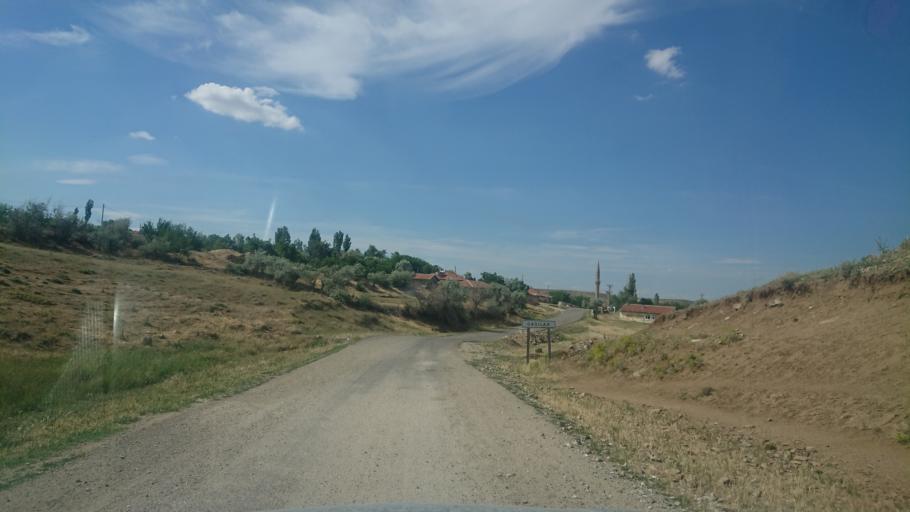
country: TR
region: Aksaray
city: Ortakoy
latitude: 38.8194
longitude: 34.0043
